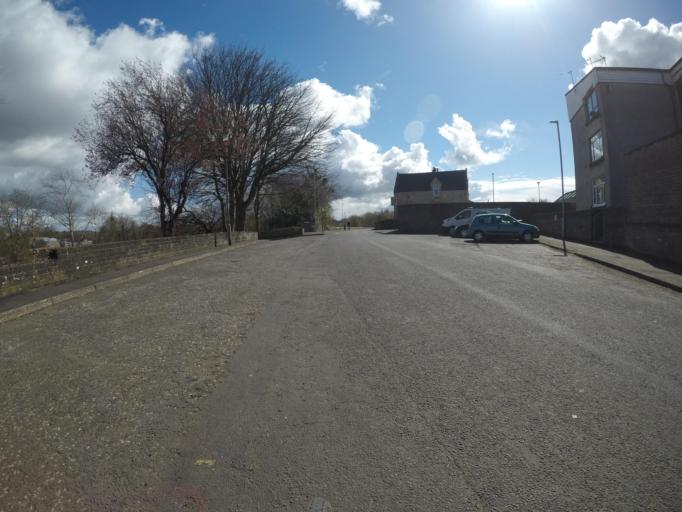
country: GB
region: Scotland
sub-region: North Ayrshire
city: Kilwinning
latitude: 55.6537
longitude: -4.6957
